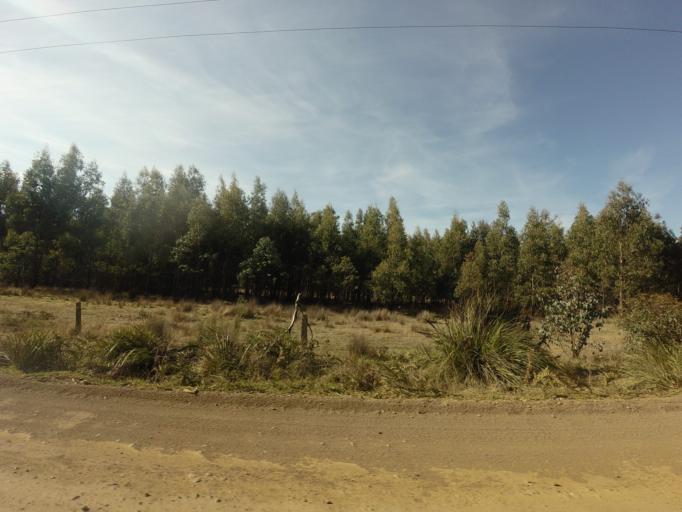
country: AU
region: Tasmania
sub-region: Sorell
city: Sorell
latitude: -42.4940
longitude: 147.5267
